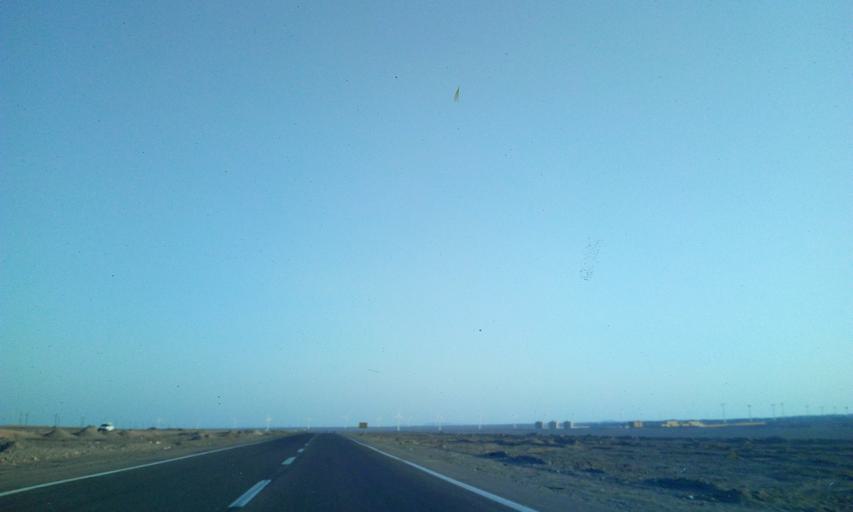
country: EG
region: South Sinai
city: Tor
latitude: 28.1044
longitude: 33.2532
